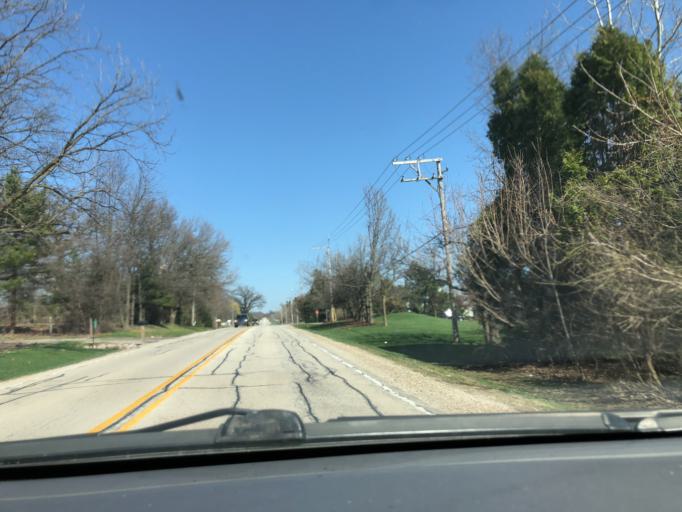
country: US
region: Illinois
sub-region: Kane County
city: Hampshire
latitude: 42.1609
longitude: -88.5162
